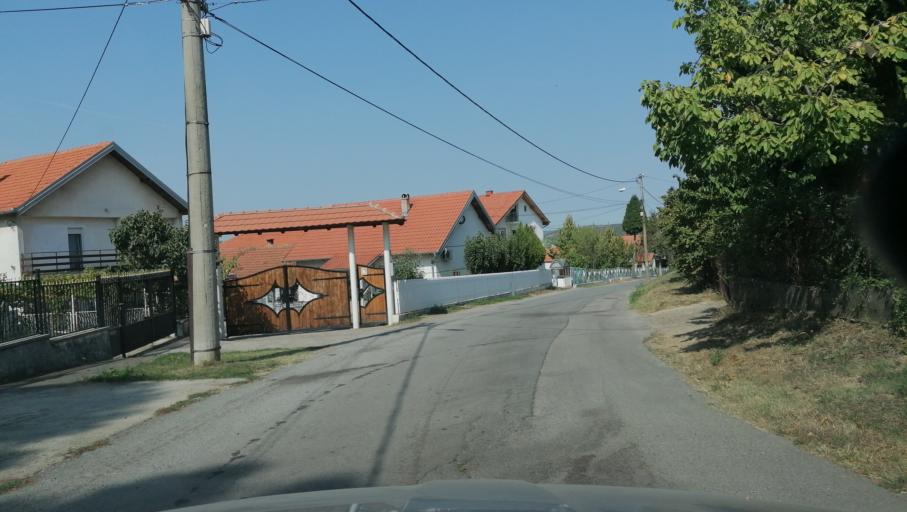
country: RS
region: Central Serbia
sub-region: Belgrade
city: Zvezdara
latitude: 44.6986
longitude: 20.5502
